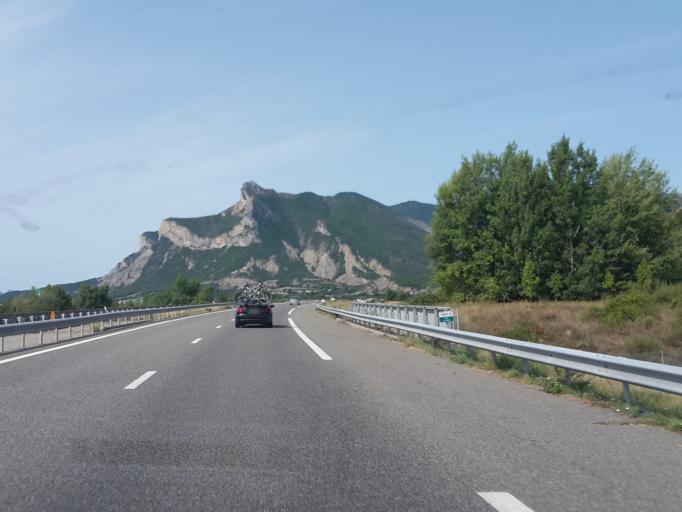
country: FR
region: Provence-Alpes-Cote d'Azur
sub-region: Departement des Hautes-Alpes
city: Tallard
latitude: 44.4193
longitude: 5.9943
